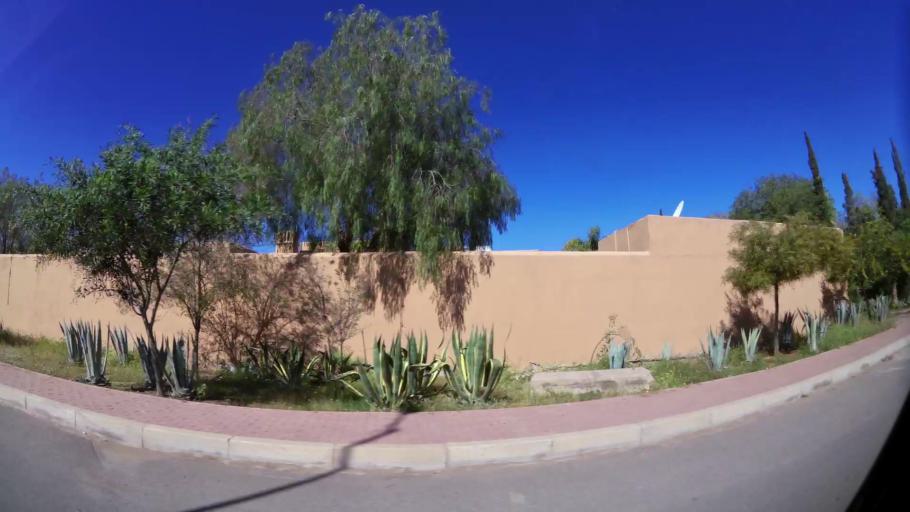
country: MA
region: Marrakech-Tensift-Al Haouz
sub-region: Marrakech
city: Marrakesh
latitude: 31.6525
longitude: -7.9357
